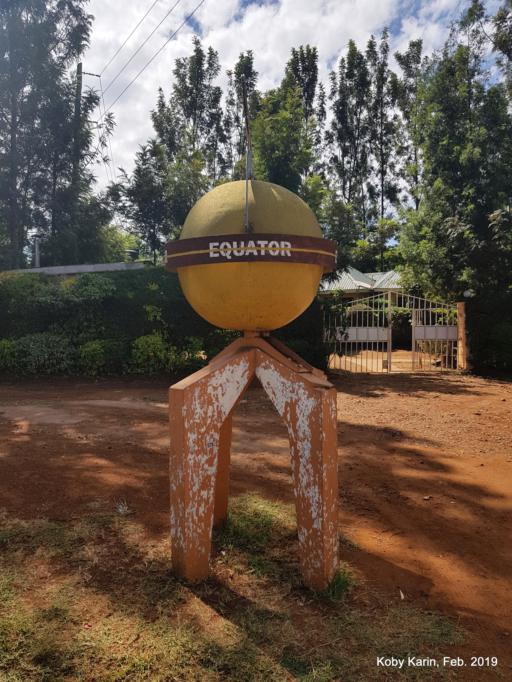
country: KE
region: Siaya
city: Yala
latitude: -0.0006
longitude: 34.6006
